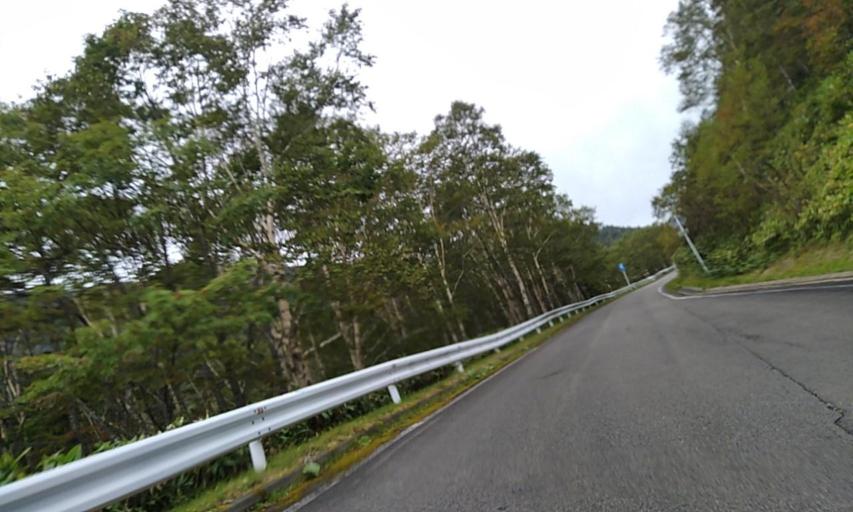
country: JP
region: Hokkaido
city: Bihoro
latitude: 43.5705
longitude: 144.2365
